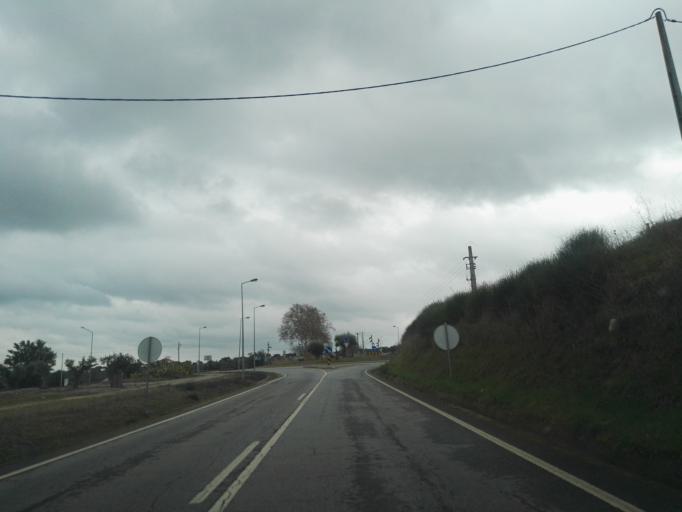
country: PT
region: Portalegre
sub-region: Arronches
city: Arronches
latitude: 39.1157
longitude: -7.2887
